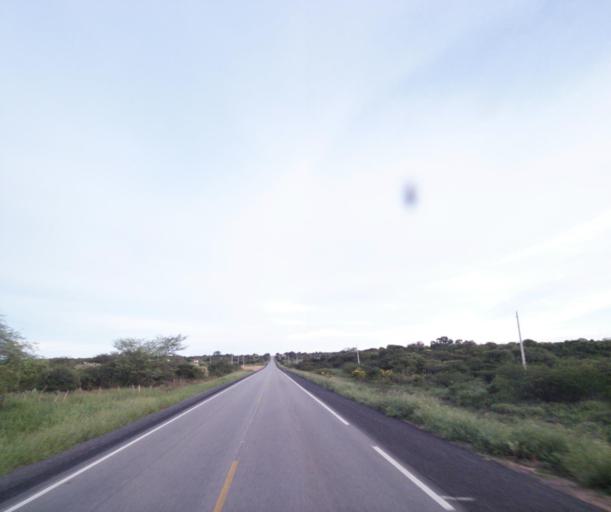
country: BR
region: Bahia
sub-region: Brumado
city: Brumado
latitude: -14.2481
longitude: -41.8586
